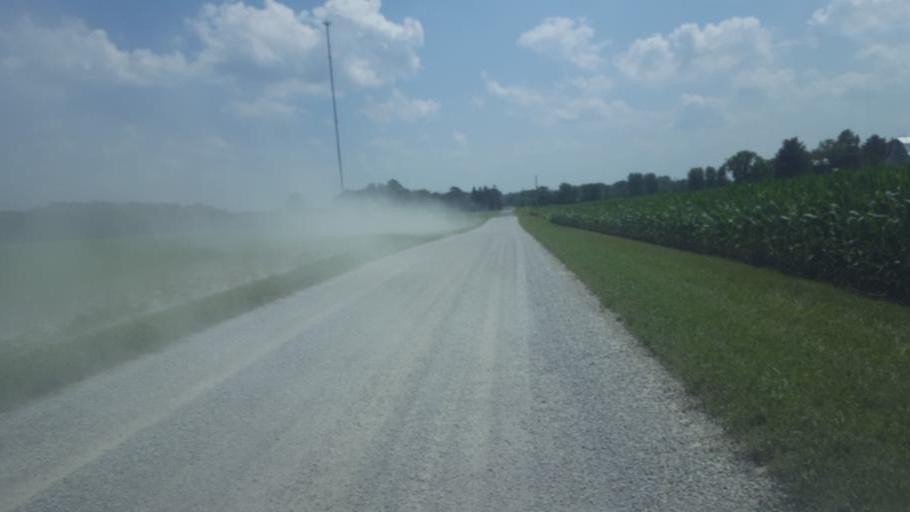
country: US
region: Ohio
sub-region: Richland County
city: Lexington
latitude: 40.6127
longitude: -82.6903
